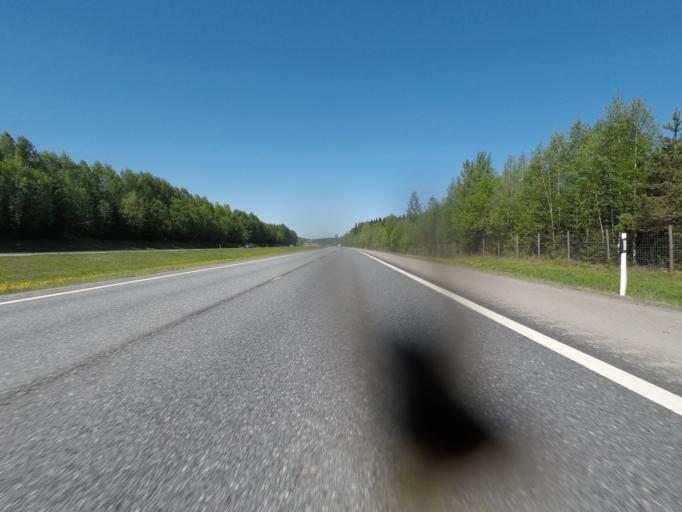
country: FI
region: Haeme
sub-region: Haemeenlinna
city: Tervakoski
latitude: 60.8383
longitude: 24.6442
